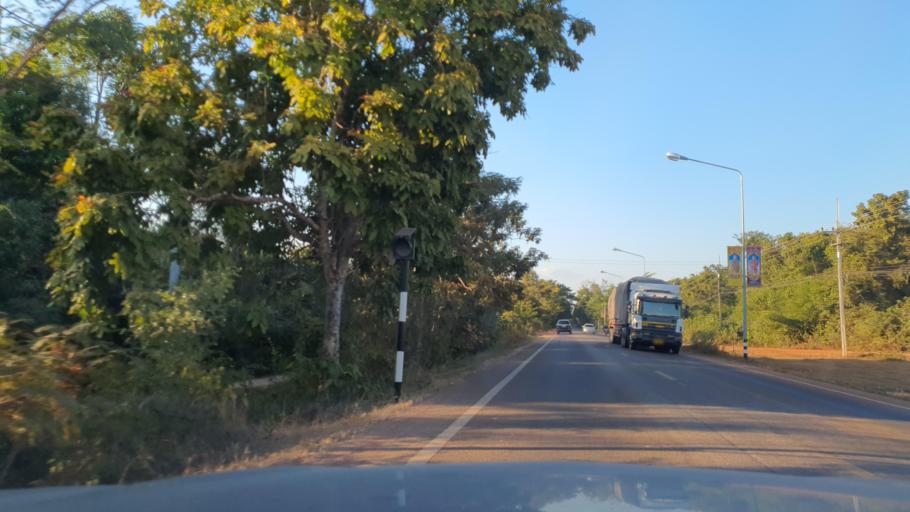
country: TH
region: Nakhon Phanom
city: Si Songkhram
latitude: 17.5603
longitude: 104.2373
